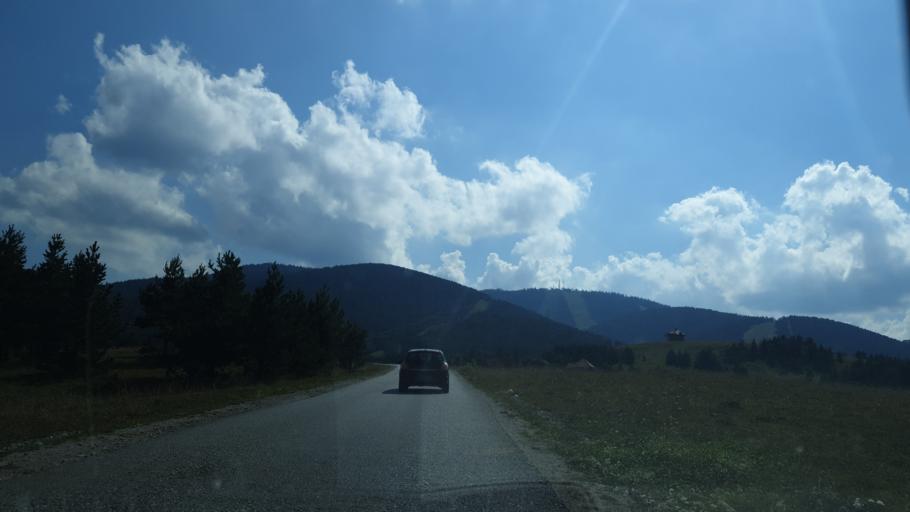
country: RS
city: Zlatibor
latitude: 43.6783
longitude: 19.6558
